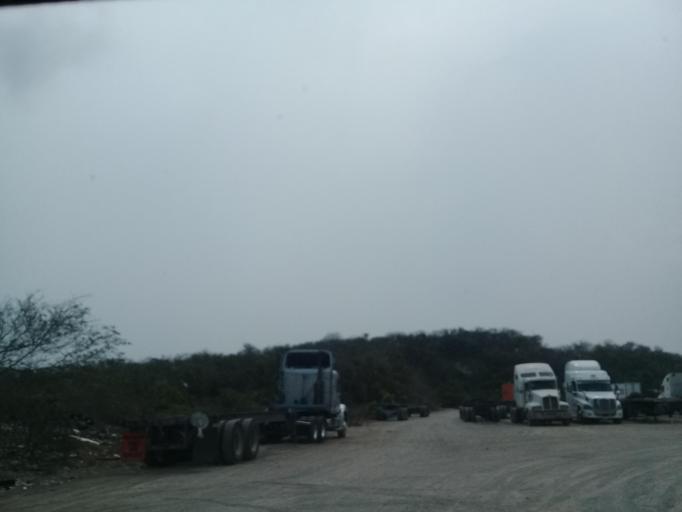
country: MX
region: Veracruz
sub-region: Veracruz
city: Colonia el Renacimiento
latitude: 19.2257
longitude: -96.2115
